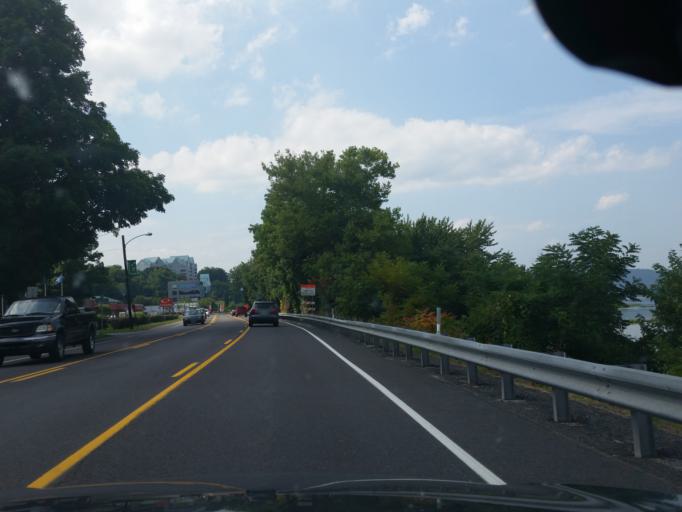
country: US
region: Pennsylvania
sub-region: Cumberland County
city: Wormleysburg
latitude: 40.2645
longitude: -76.9085
